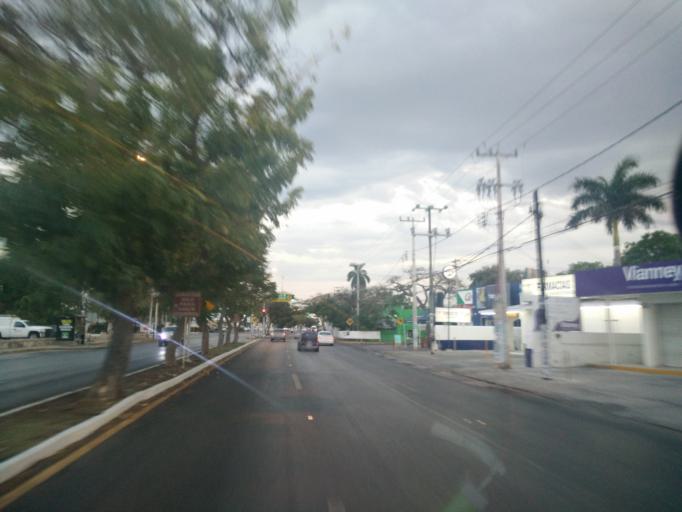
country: MX
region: Yucatan
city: Merida
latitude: 20.9609
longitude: -89.6419
